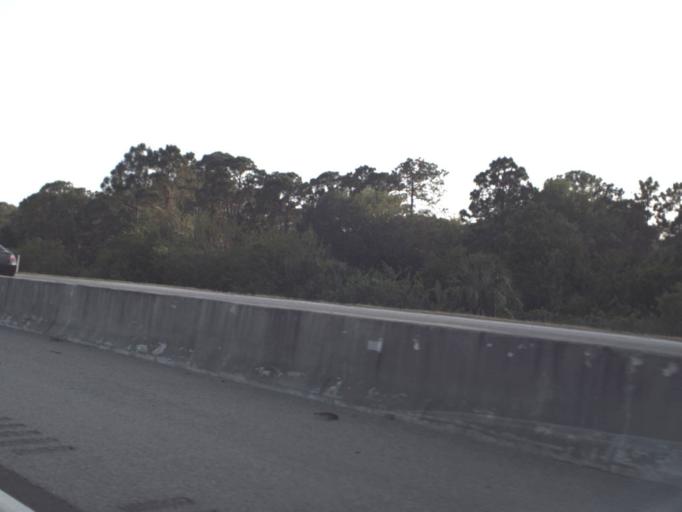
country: US
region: Florida
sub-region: Brevard County
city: Sharpes
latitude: 28.4065
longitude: -80.8204
